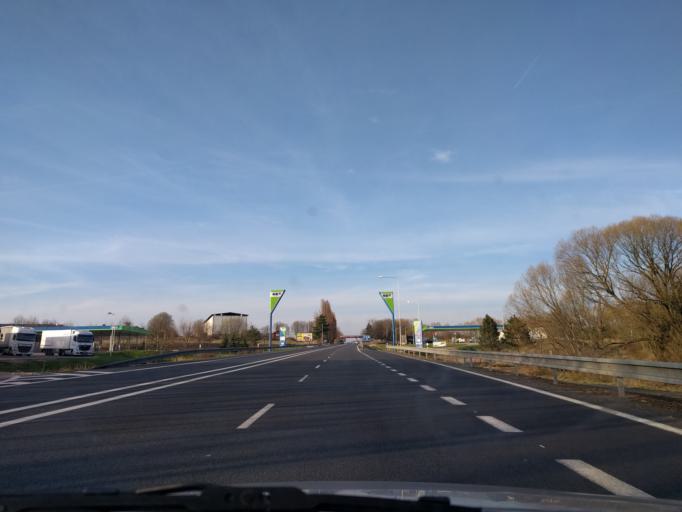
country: CZ
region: Central Bohemia
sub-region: Okres Benesov
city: Cercany
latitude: 49.8836
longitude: 14.7088
